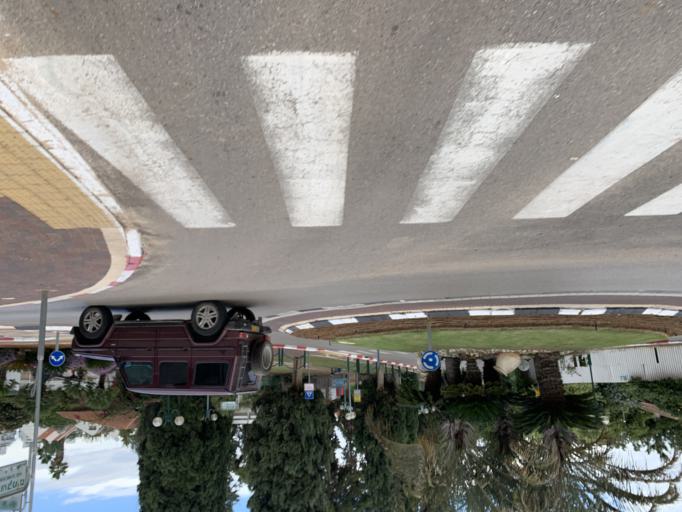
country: IL
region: Central District
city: Hod HaSharon
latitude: 32.1559
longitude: 34.8870
